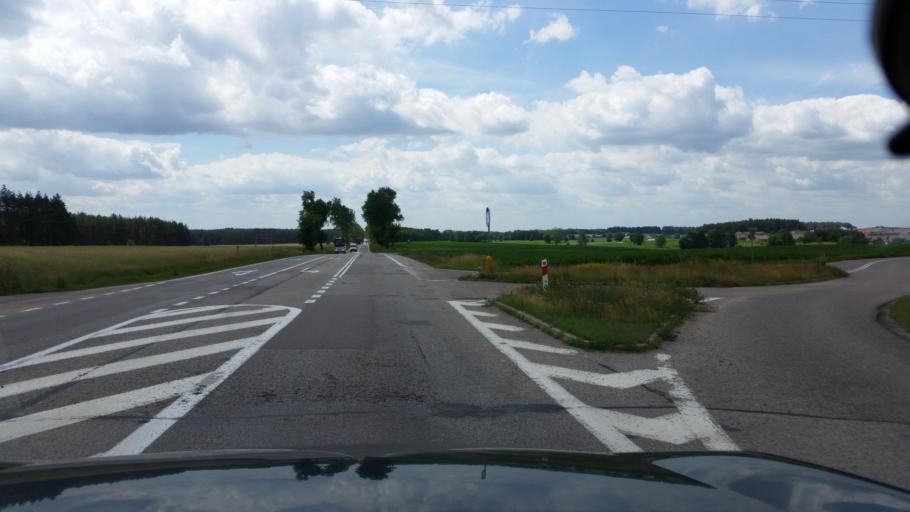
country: PL
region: Podlasie
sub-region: Powiat kolnenski
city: Stawiski
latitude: 53.3227
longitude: 22.1528
